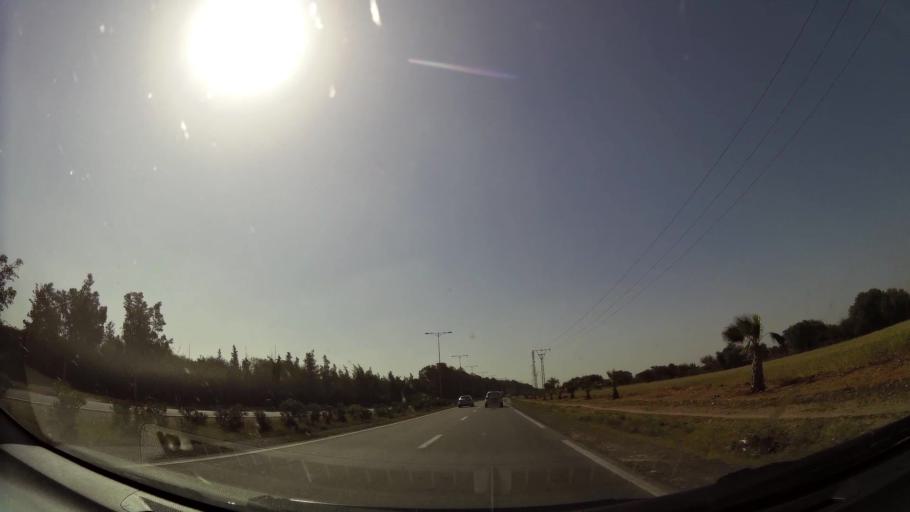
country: MA
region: Souss-Massa-Draa
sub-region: Inezgane-Ait Mellou
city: Inezgane
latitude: 30.3504
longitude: -9.4804
